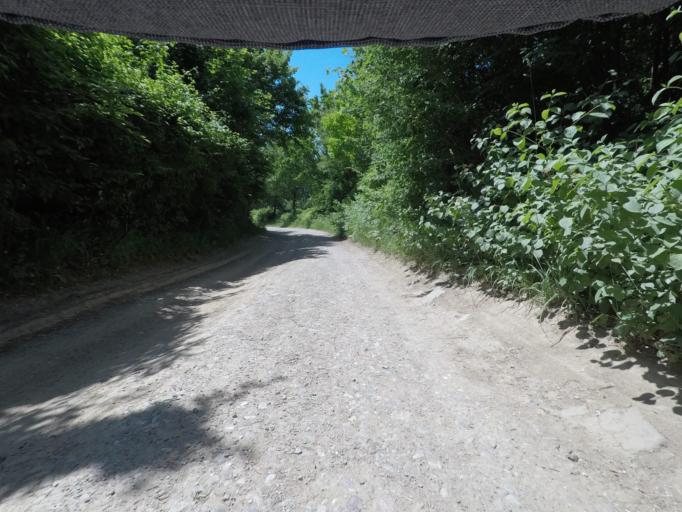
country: AT
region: Lower Austria
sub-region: Politischer Bezirk Modling
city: Perchtoldsdorf
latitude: 48.1767
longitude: 16.2528
